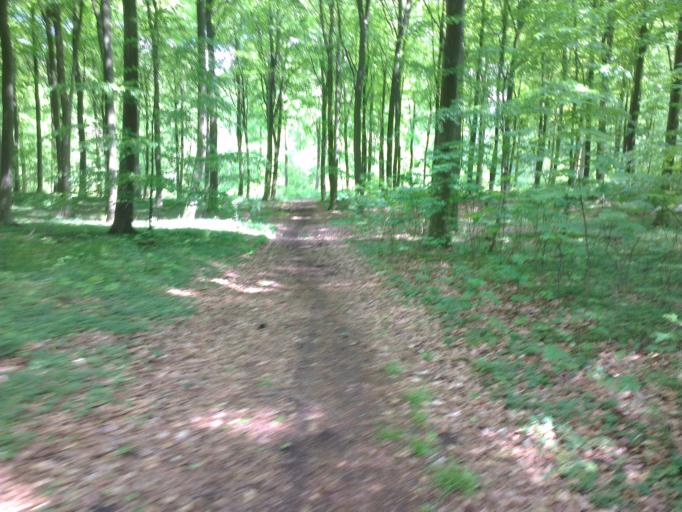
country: DK
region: Capital Region
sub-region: Frederikssund Kommune
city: Frederikssund
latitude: 55.8429
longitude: 12.0221
